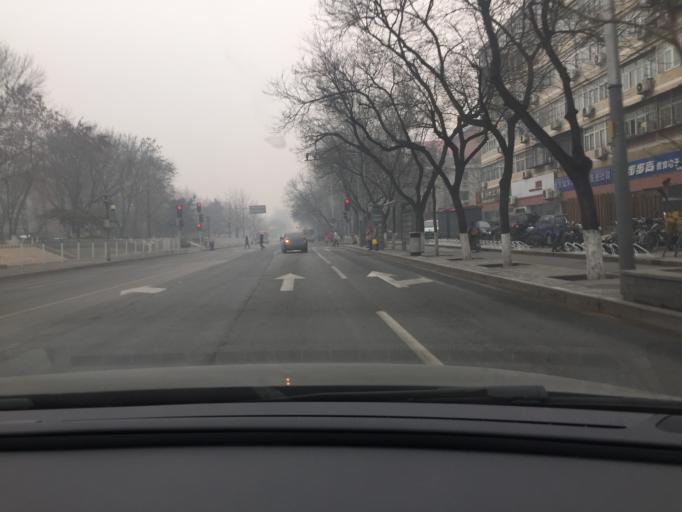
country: CN
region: Beijing
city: Jingshan
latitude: 39.9192
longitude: 116.4002
